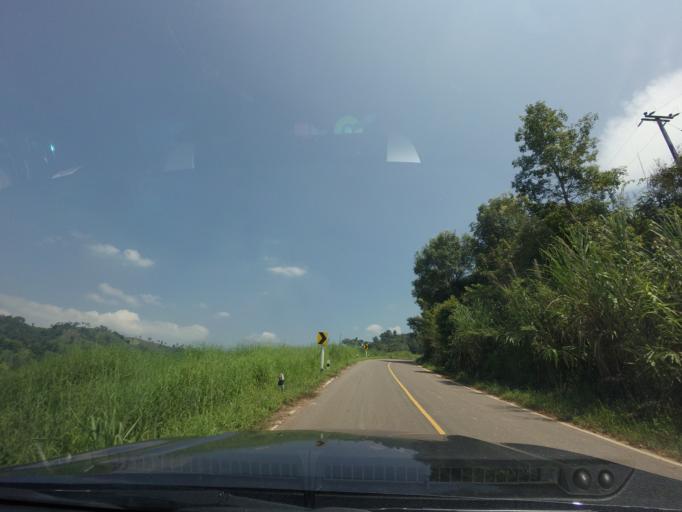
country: TH
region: Loei
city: Na Haeo
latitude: 17.5681
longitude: 100.8924
